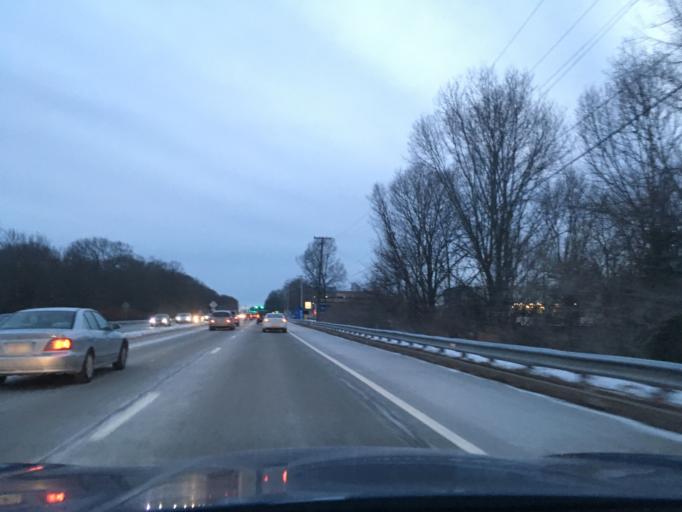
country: US
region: Rhode Island
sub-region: Kent County
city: West Warwick
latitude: 41.6955
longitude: -71.4981
